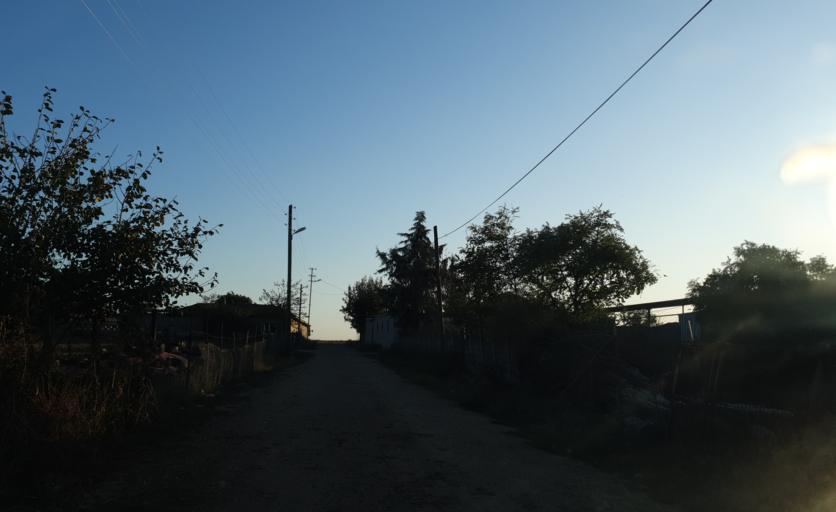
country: TR
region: Tekirdag
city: Beyazkoy
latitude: 41.3297
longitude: 27.7468
